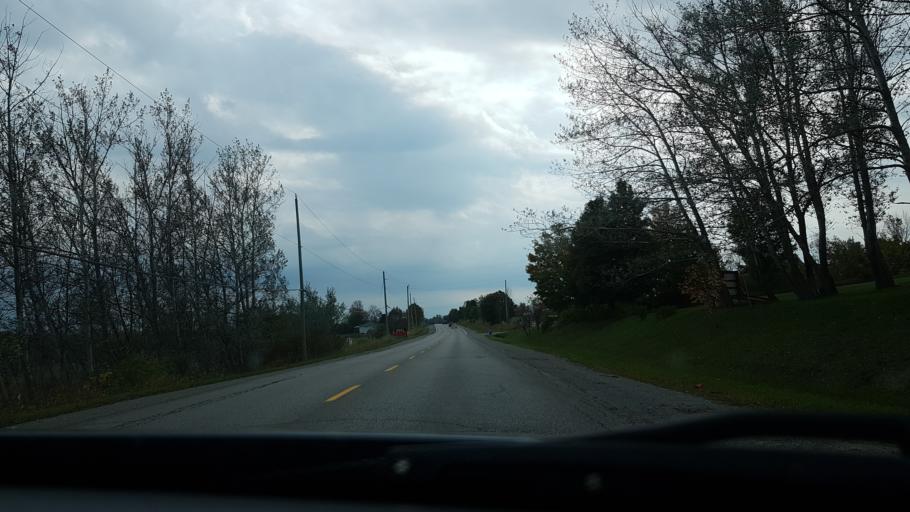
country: CA
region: Ontario
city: Omemee
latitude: 44.4993
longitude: -78.7431
